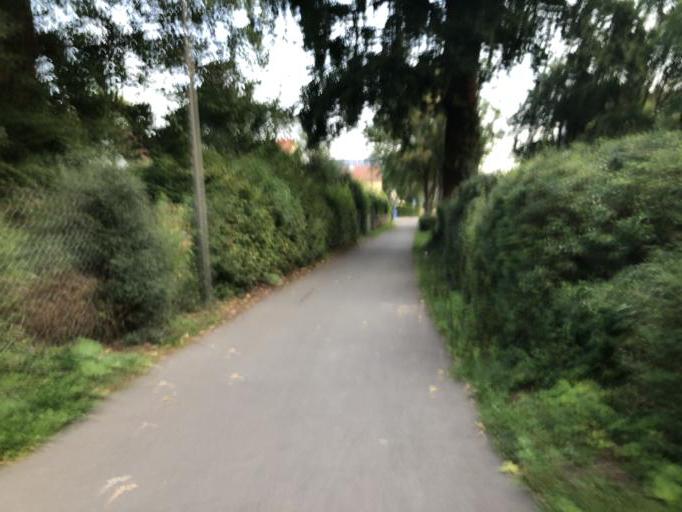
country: DE
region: Bavaria
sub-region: Regierungsbezirk Mittelfranken
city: Erlangen
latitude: 49.5880
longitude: 10.9597
